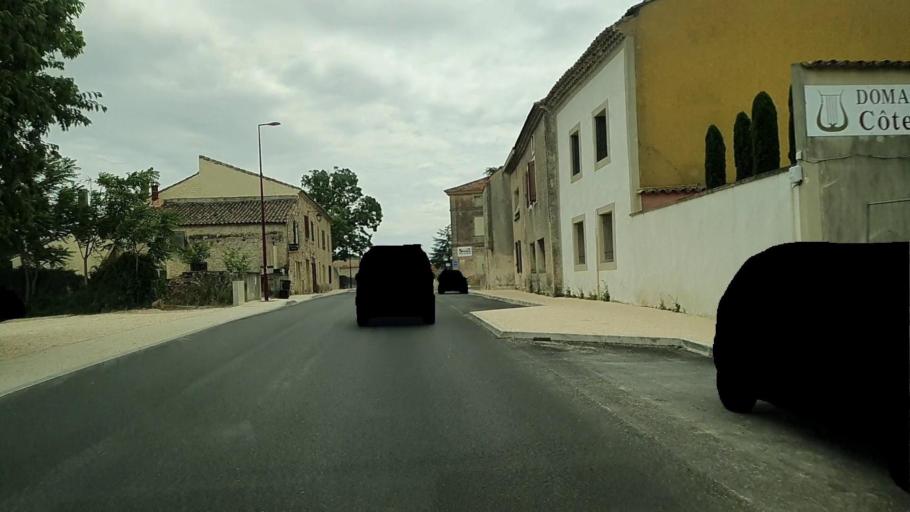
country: FR
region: Languedoc-Roussillon
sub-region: Departement du Gard
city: Connaux
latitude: 44.0407
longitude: 4.5809
